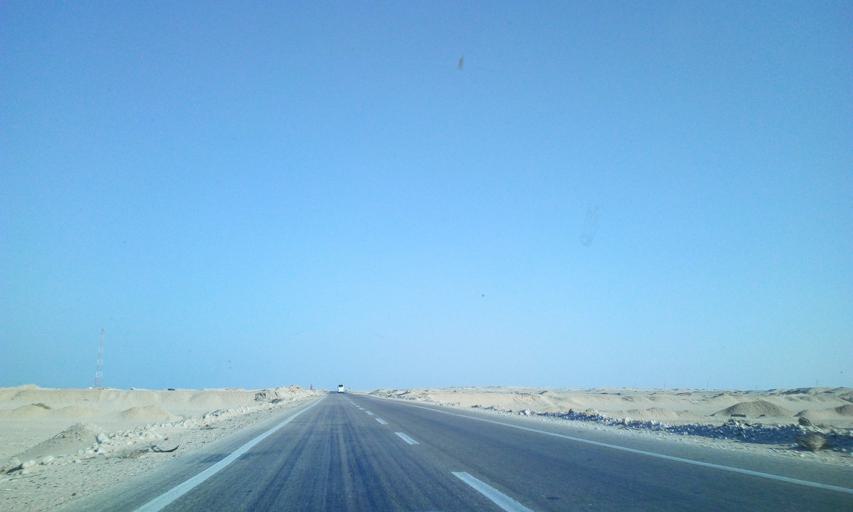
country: EG
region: As Suways
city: Ain Sukhna
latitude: 28.8664
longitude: 32.6724
